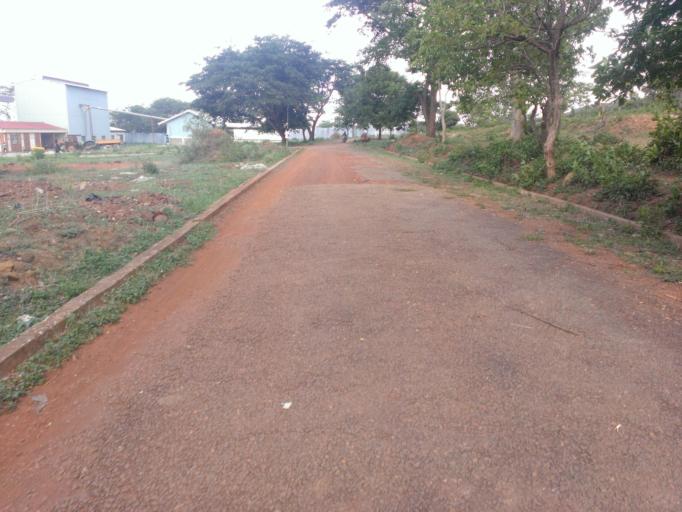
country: UG
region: Eastern Region
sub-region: Busia District
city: Busia
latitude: 0.5443
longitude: 34.0206
